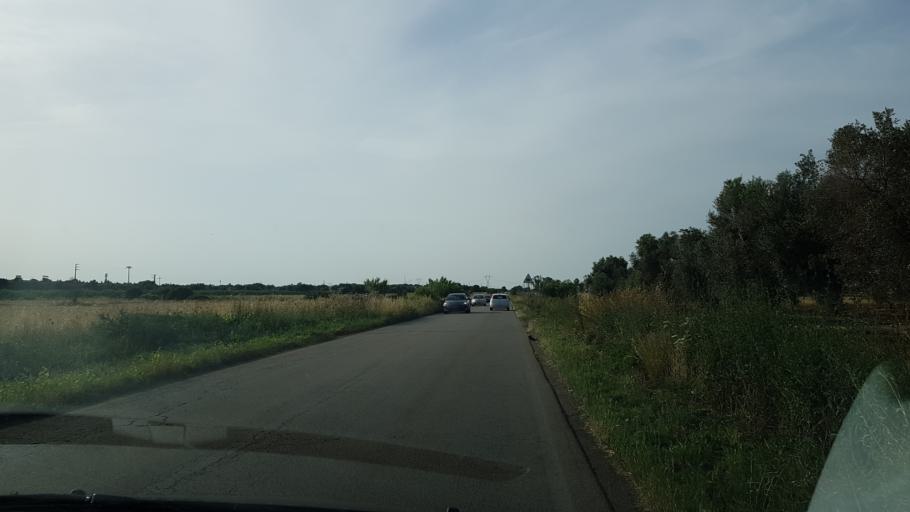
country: IT
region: Apulia
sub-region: Provincia di Lecce
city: Porto Cesareo
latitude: 40.3309
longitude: 17.8523
